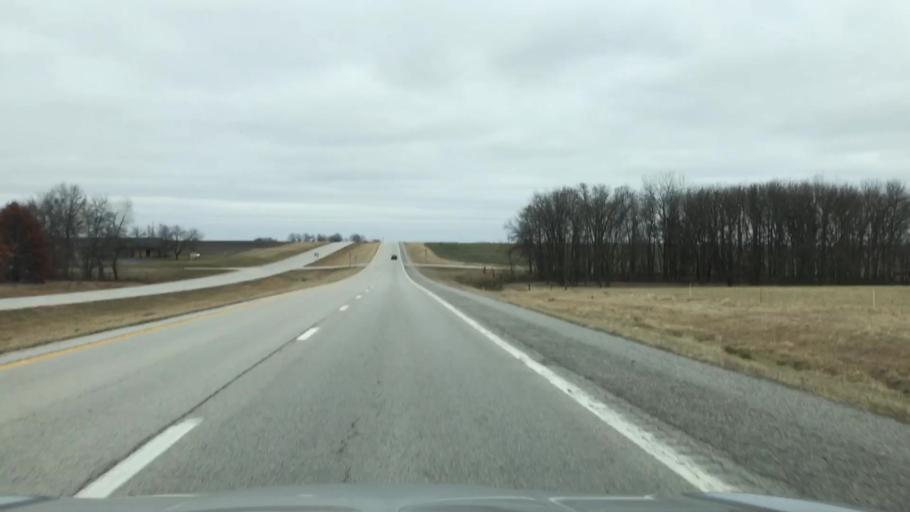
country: US
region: Missouri
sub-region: Livingston County
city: Chillicothe
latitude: 39.7761
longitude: -93.4846
